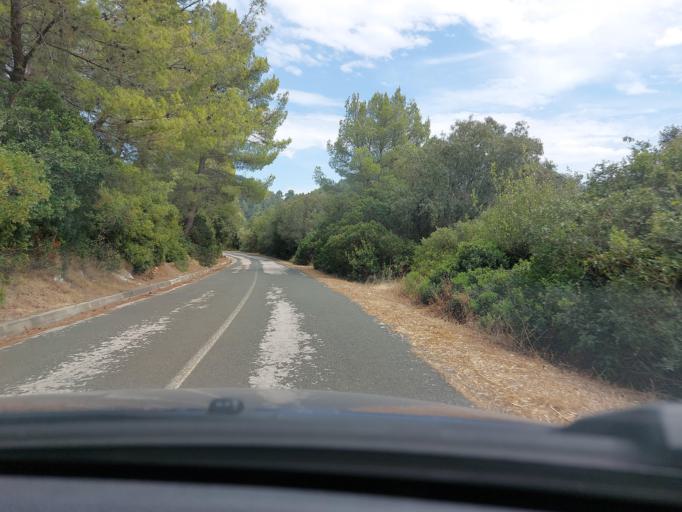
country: HR
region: Dubrovacko-Neretvanska
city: Smokvica
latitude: 42.7611
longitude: 16.8995
